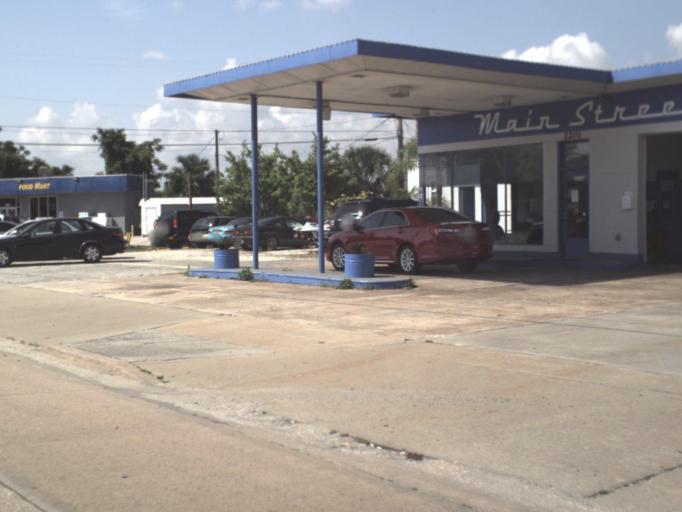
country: US
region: Florida
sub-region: Saint Johns County
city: Saint Augustine
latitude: 29.9133
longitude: -81.3234
